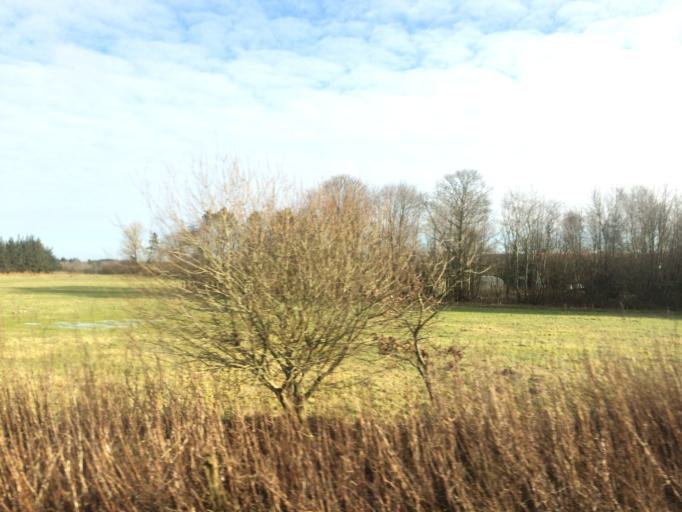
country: DK
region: South Denmark
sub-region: Vejle Kommune
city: Give
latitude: 55.8698
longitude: 9.2420
